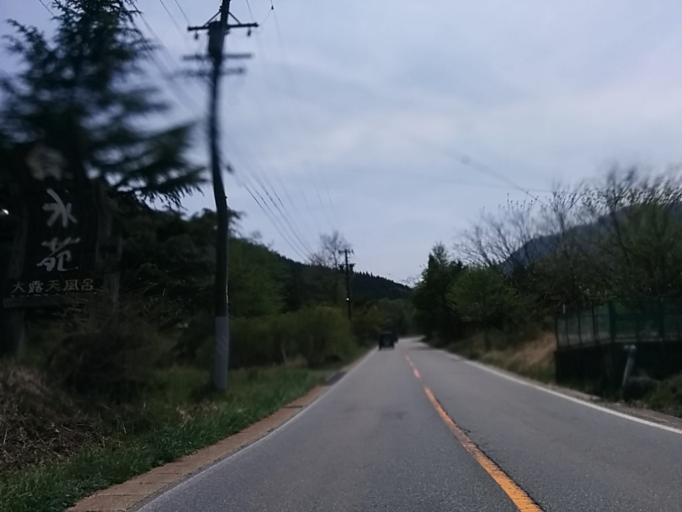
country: JP
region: Gifu
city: Takayama
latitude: 36.2324
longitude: 137.5335
